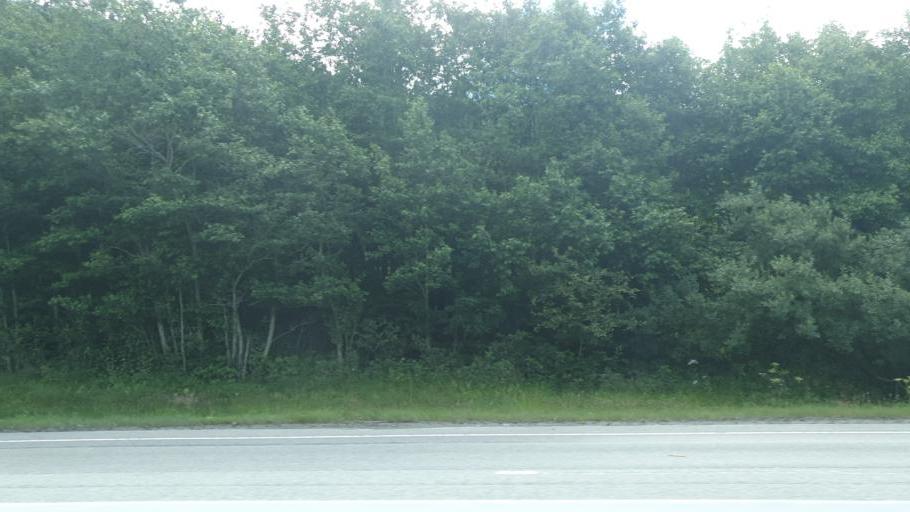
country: NO
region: Sor-Trondelag
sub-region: Melhus
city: Melhus
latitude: 63.2518
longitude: 10.2799
